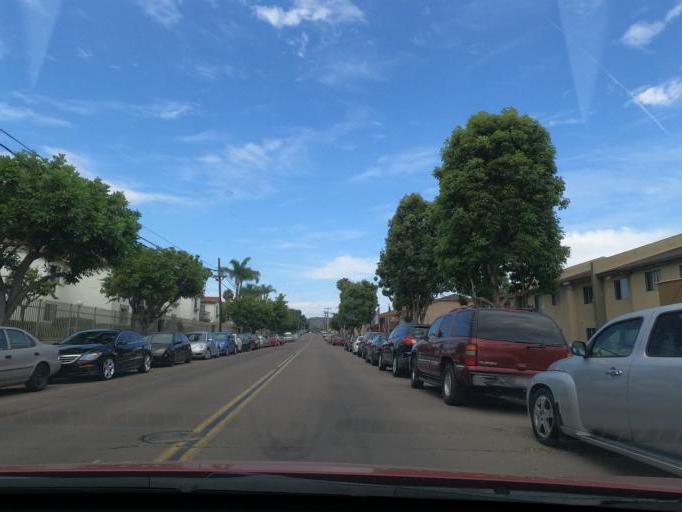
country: US
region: California
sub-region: San Diego County
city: Imperial Beach
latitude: 32.5582
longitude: -117.0575
